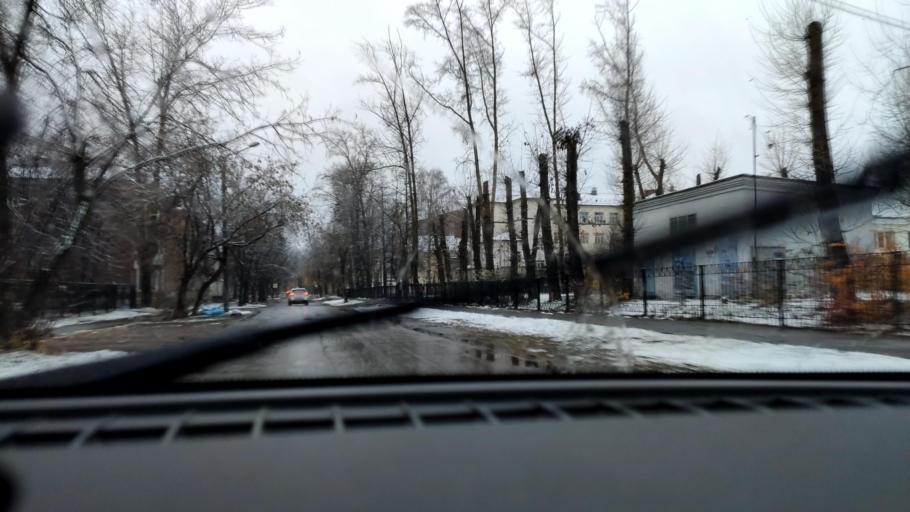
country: RU
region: Perm
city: Kultayevo
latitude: 58.0001
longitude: 55.9460
